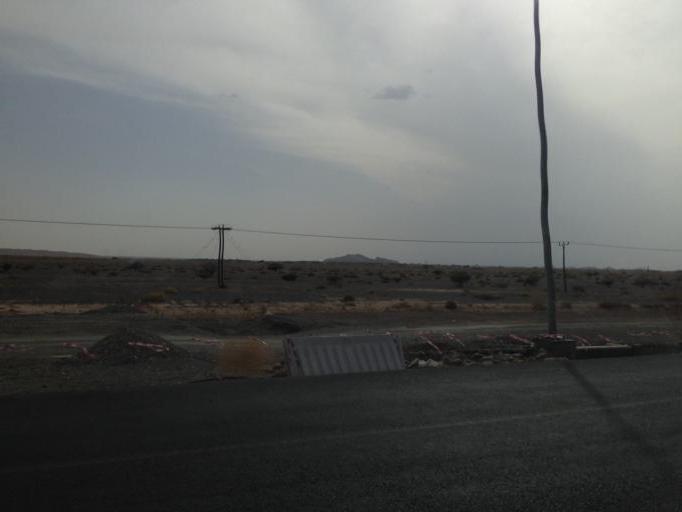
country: OM
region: Ash Sharqiyah
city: Al Qabil
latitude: 22.5524
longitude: 58.7170
